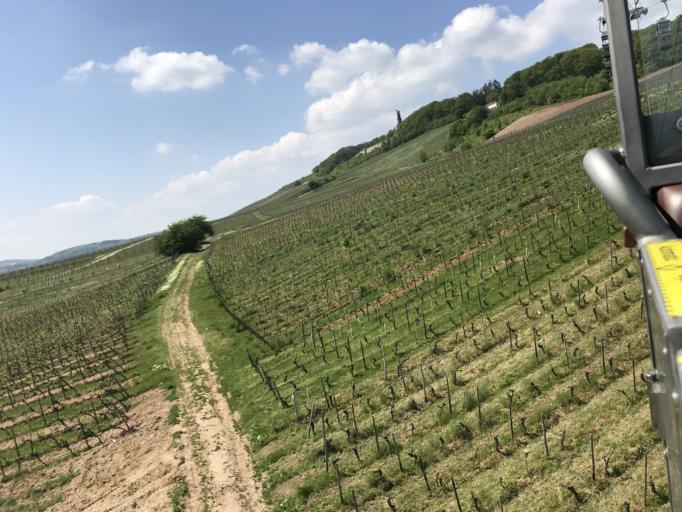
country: DE
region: Rheinland-Pfalz
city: Bingen am Rhein
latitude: 49.9816
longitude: 7.9100
